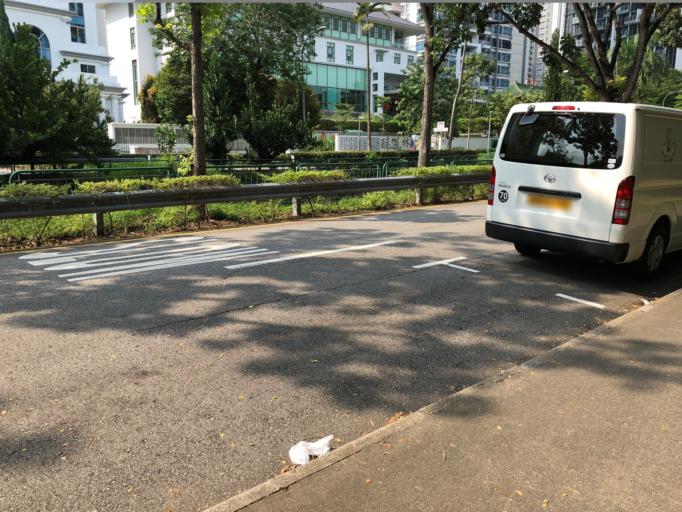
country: SG
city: Singapore
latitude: 1.3131
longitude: 103.8411
